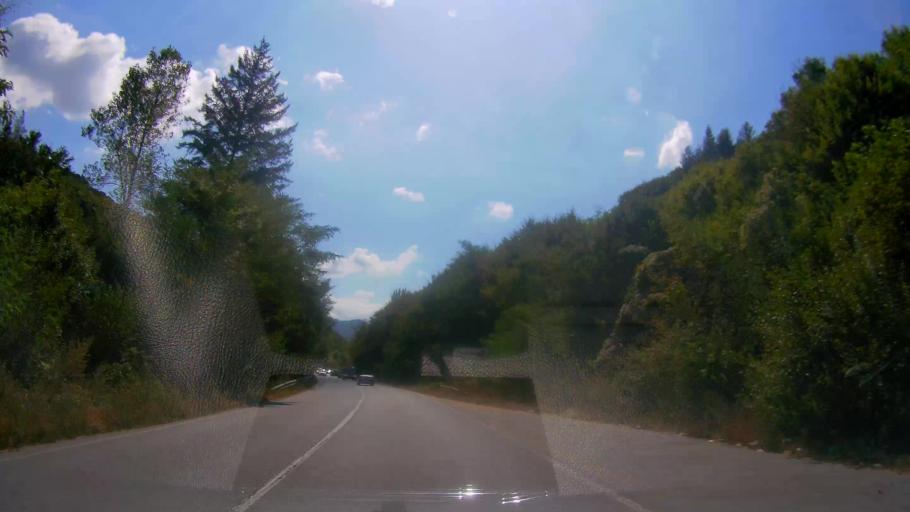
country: BG
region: Stara Zagora
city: Gurkovo
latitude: 42.7464
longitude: 25.7092
